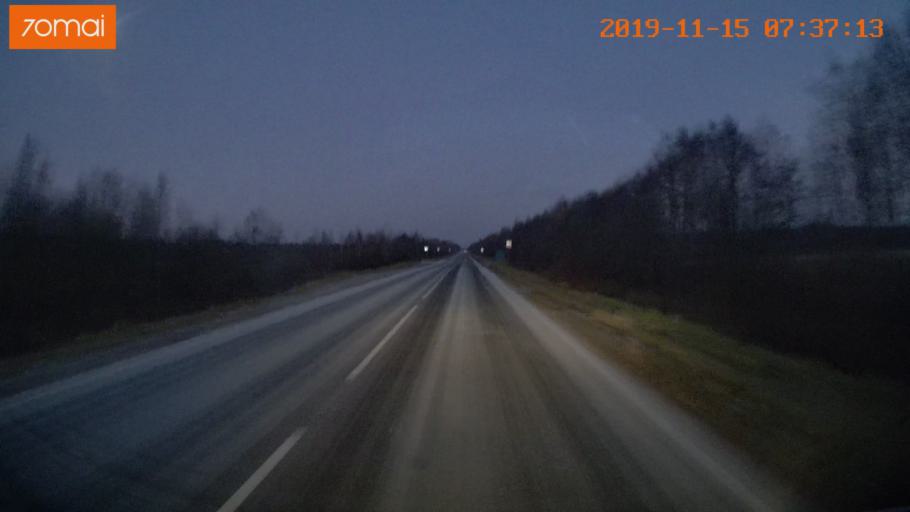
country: RU
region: Vologda
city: Sheksna
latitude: 58.7466
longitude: 38.4218
